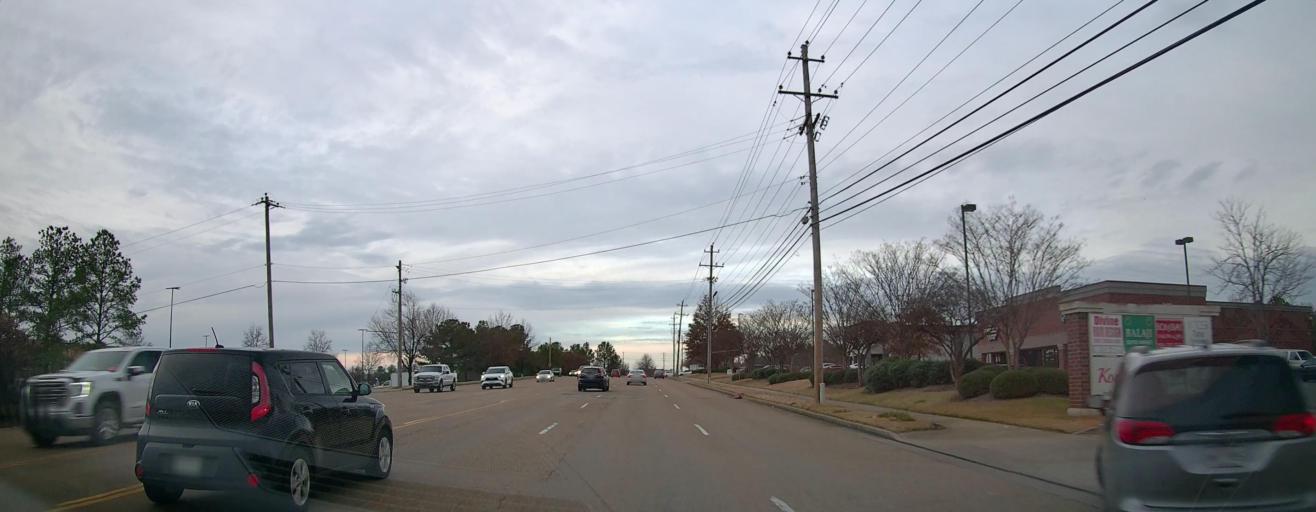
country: US
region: Tennessee
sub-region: Shelby County
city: Germantown
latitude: 35.0446
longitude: -89.7959
